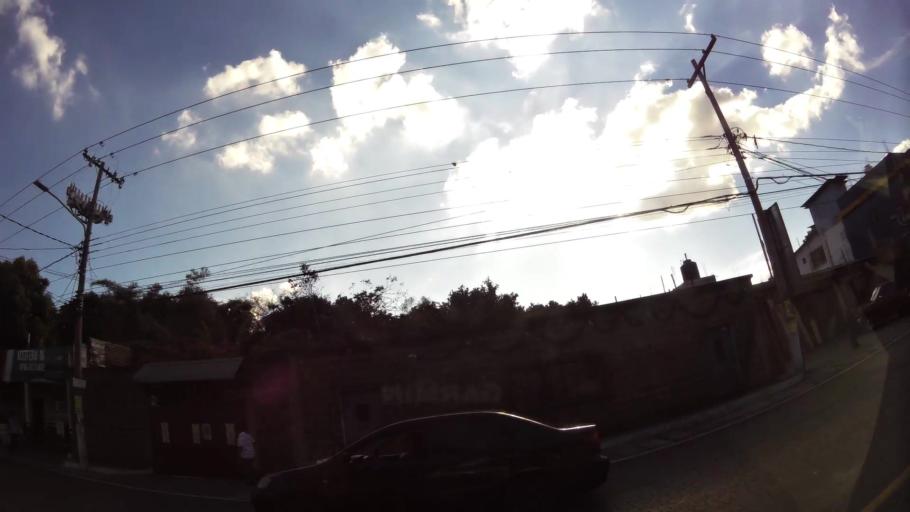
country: GT
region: Guatemala
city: Villa Nueva
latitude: 14.5178
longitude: -90.5796
